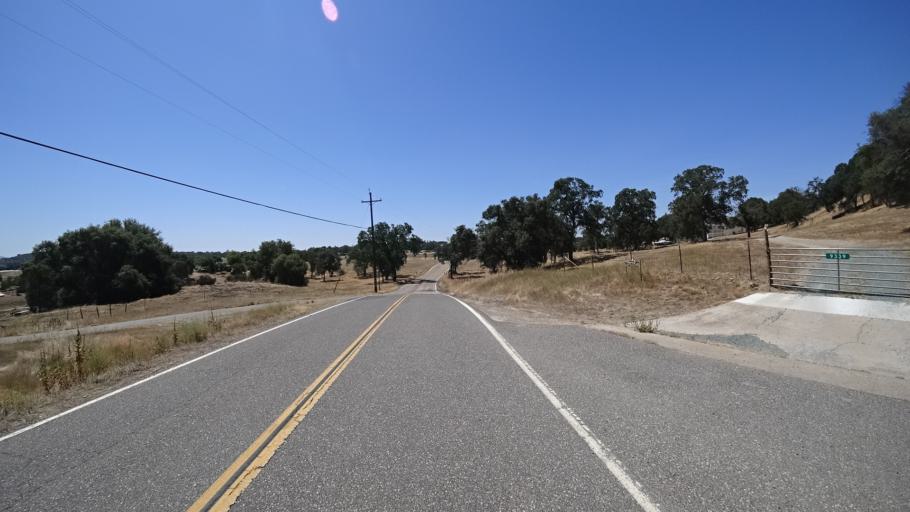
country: US
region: California
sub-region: Calaveras County
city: Rancho Calaveras
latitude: 38.1629
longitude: -120.9552
